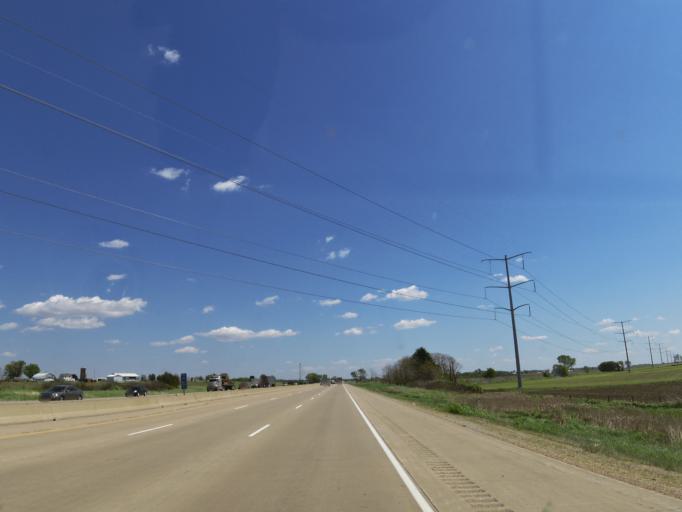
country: US
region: Wisconsin
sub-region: Dane County
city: De Forest
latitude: 43.2854
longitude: -89.4087
